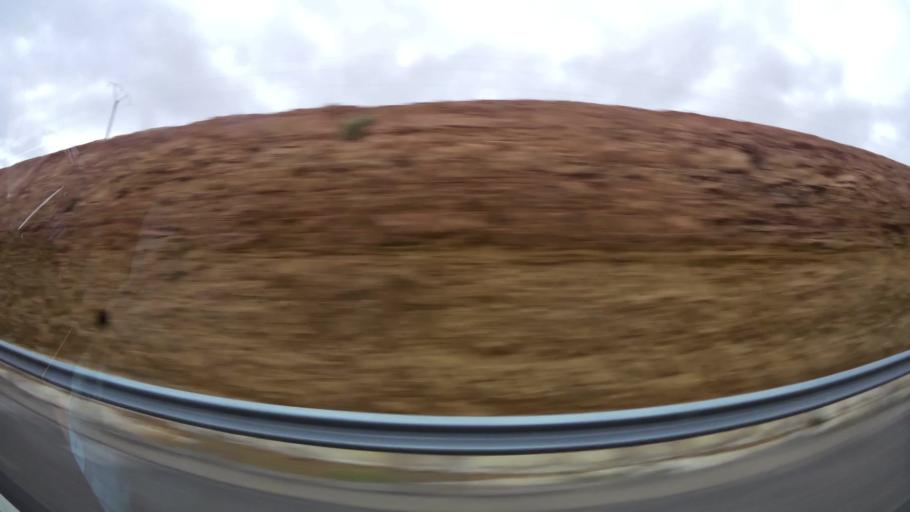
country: MA
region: Taza-Al Hoceima-Taounate
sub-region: Taza
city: Guercif
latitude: 34.3039
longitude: -3.6792
